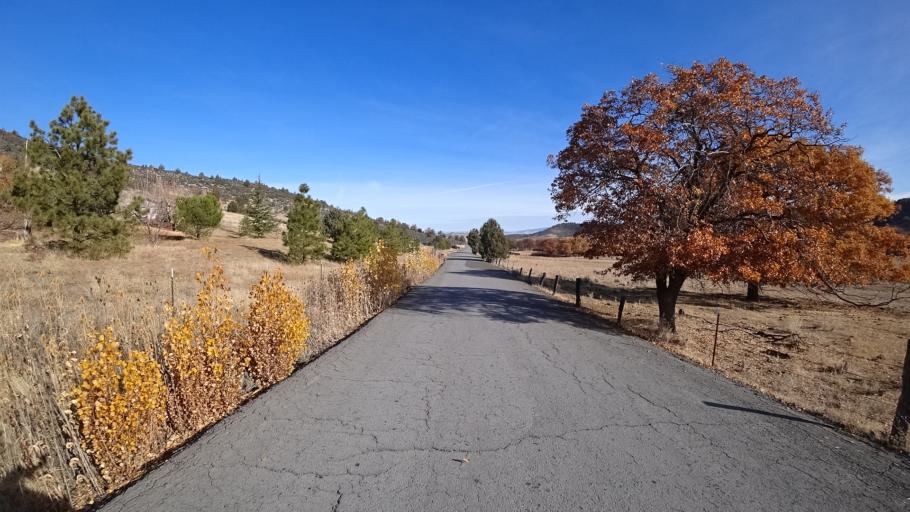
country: US
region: California
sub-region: Siskiyou County
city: Montague
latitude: 41.6260
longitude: -122.5732
